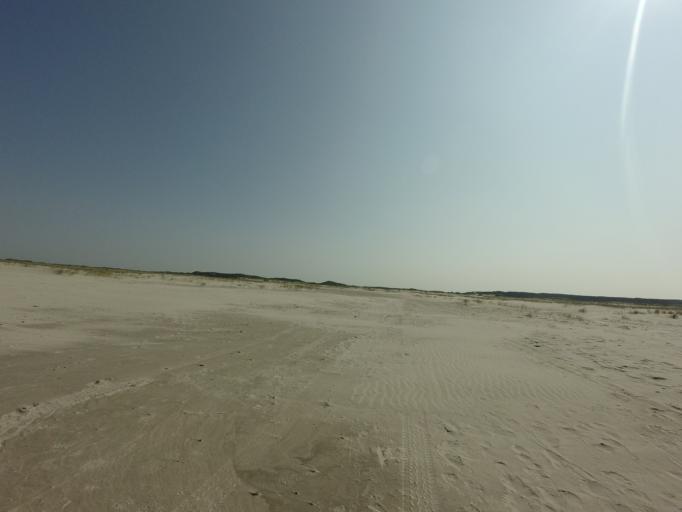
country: NL
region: Friesland
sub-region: Gemeente Schiermonnikoog
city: Schiermonnikoog
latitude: 53.5043
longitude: 6.2446
